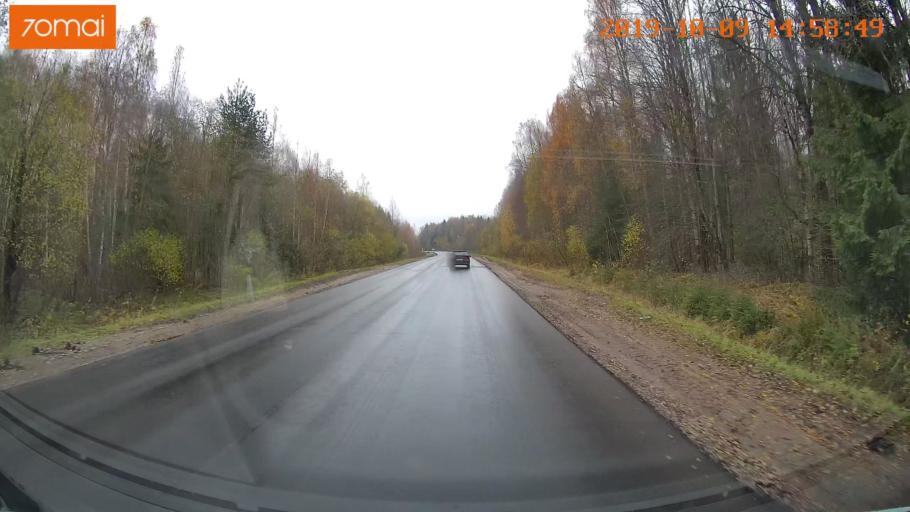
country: RU
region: Kostroma
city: Chistyye Bory
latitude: 58.3242
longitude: 41.6587
